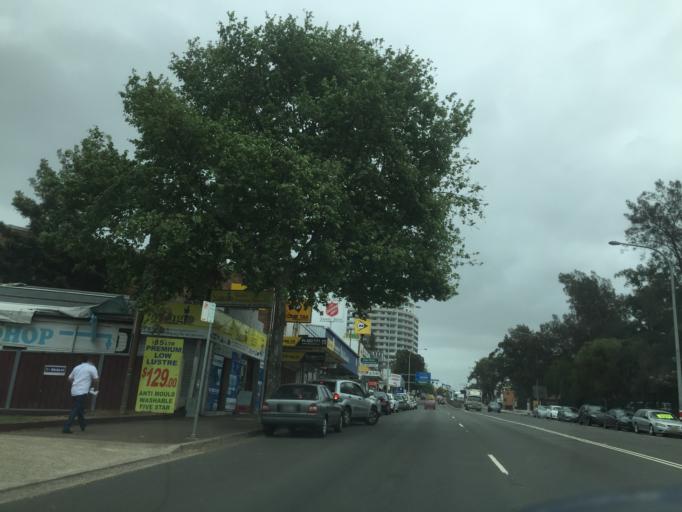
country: AU
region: New South Wales
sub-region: Blacktown
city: Blacktown
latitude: -33.7732
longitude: 150.9140
